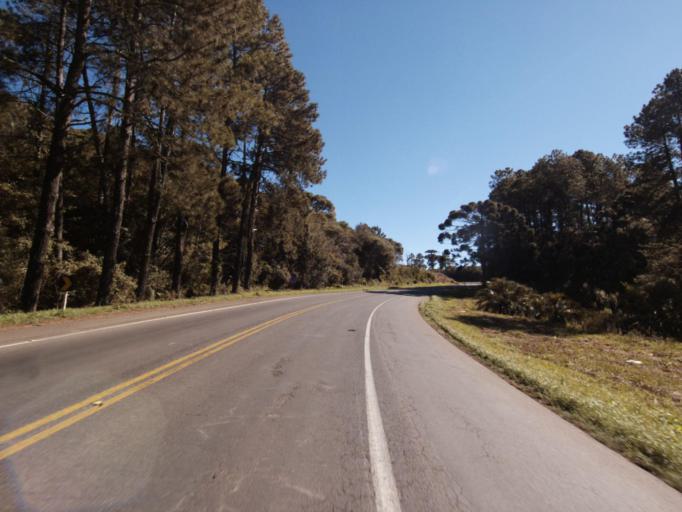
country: BR
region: Santa Catarina
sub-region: Joacaba
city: Joacaba
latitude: -27.1609
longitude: -51.5734
